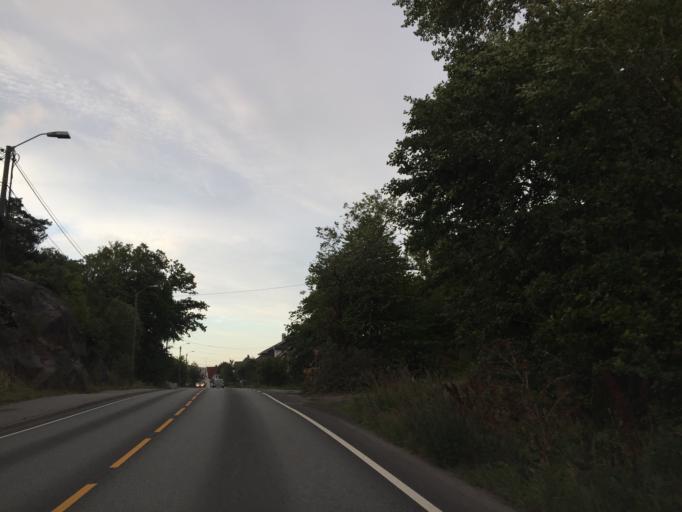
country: NO
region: Ostfold
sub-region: Fredrikstad
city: Fredrikstad
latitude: 59.1933
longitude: 10.9401
